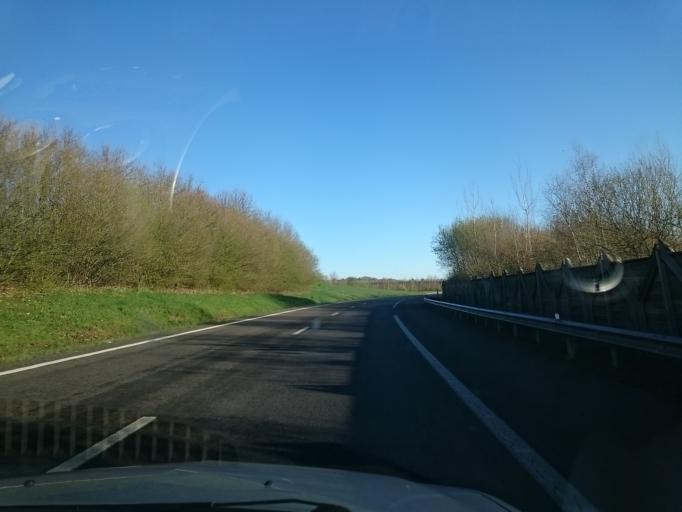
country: FR
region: Brittany
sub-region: Departement d'Ille-et-Vilaine
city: Fouillard
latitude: 48.1527
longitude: -1.6004
